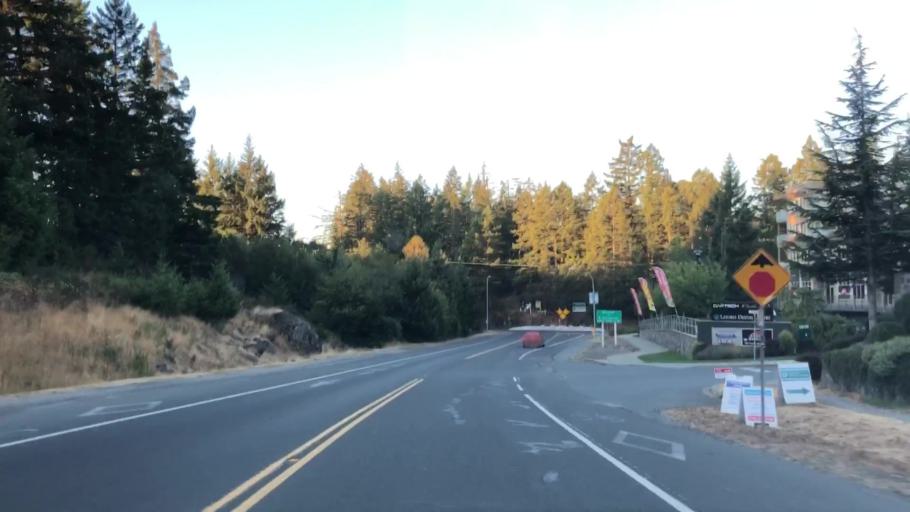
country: CA
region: British Columbia
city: Colwood
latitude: 48.4096
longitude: -123.5075
